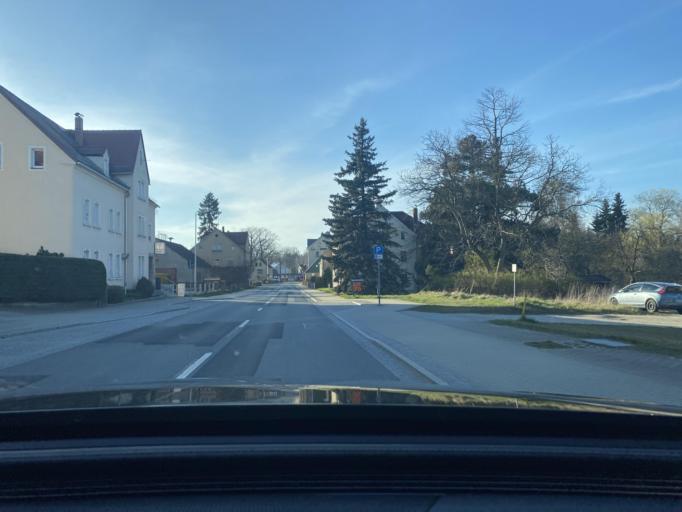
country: DE
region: Saxony
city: Grosspostwitz
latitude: 51.1151
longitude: 14.4435
